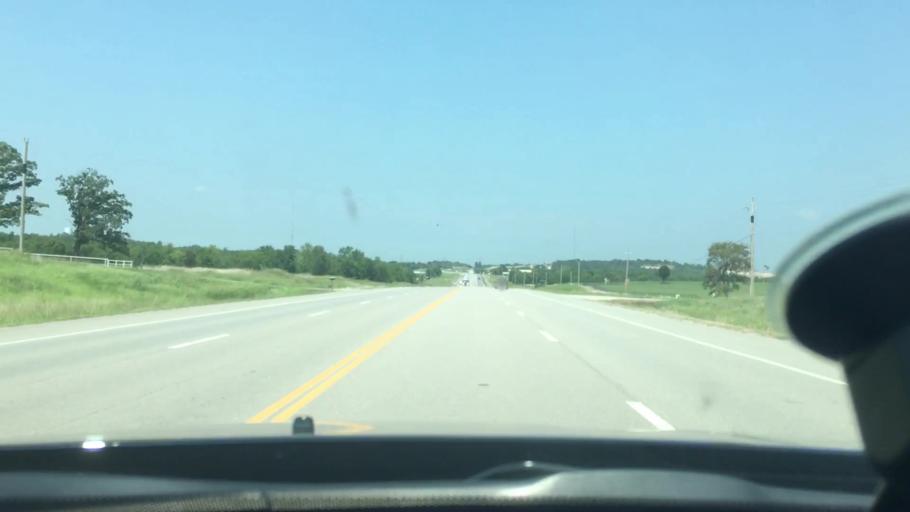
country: US
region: Oklahoma
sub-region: Atoka County
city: Atoka
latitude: 34.3622
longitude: -96.0974
